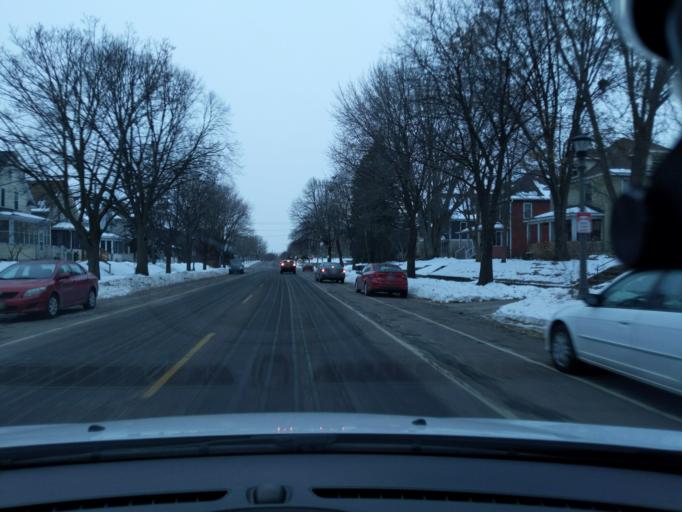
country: US
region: Minnesota
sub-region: Ramsey County
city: Falcon Heights
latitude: 44.9629
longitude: -93.1755
